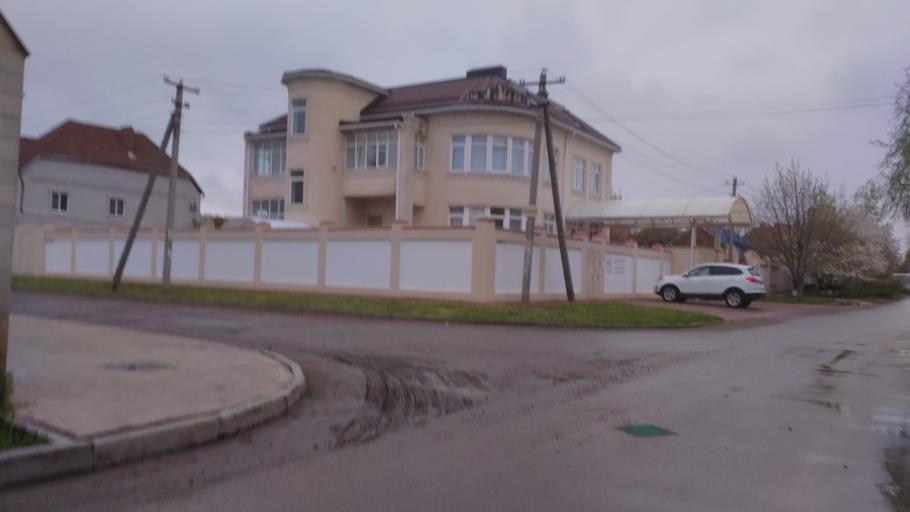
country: RU
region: Krasnodarskiy
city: Krasnodar
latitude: 45.0742
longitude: 39.0124
